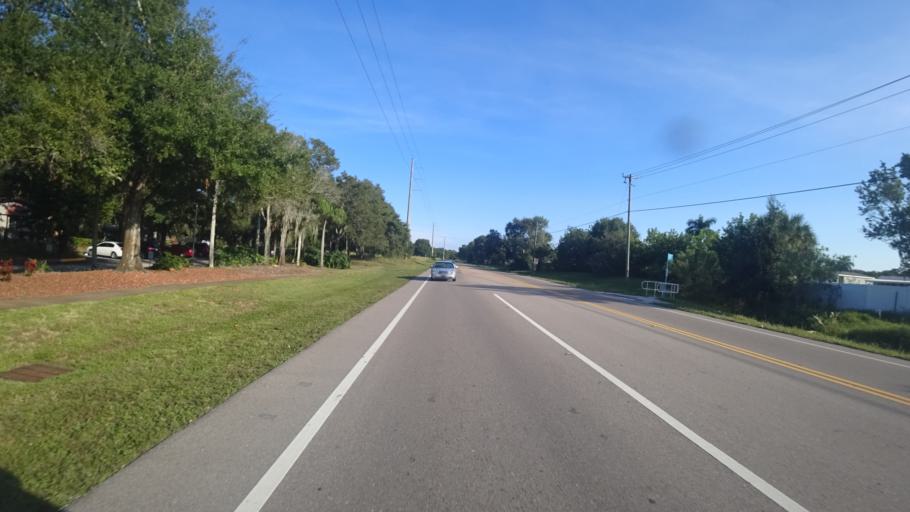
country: US
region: Florida
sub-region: Manatee County
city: West Samoset
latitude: 27.4588
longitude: -82.5525
